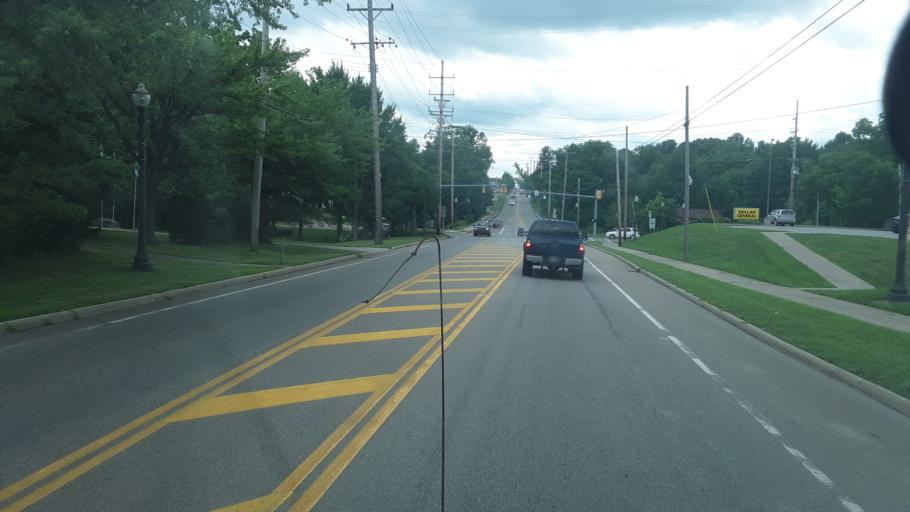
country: US
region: Ohio
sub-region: Ashtabula County
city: Jefferson
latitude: 41.7473
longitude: -80.7695
